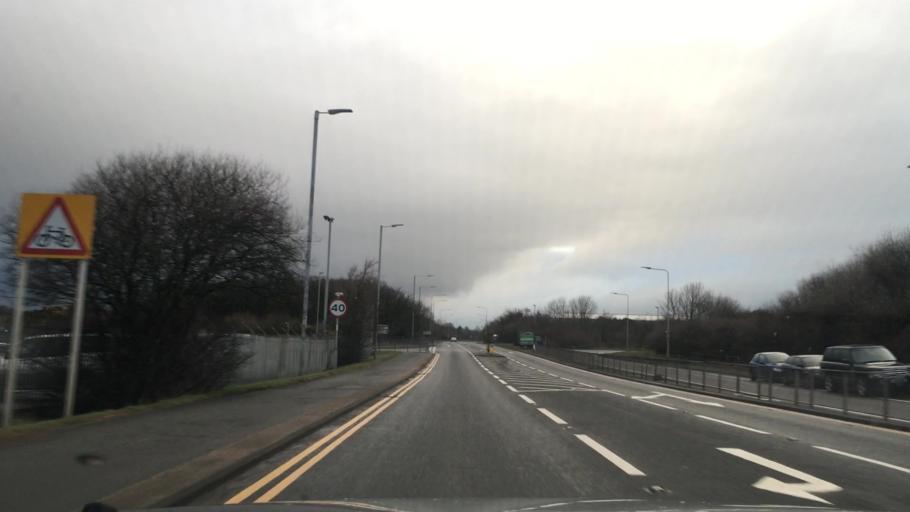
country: GB
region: England
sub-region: Cumbria
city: Barrow in Furness
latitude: 54.1457
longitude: -3.2303
